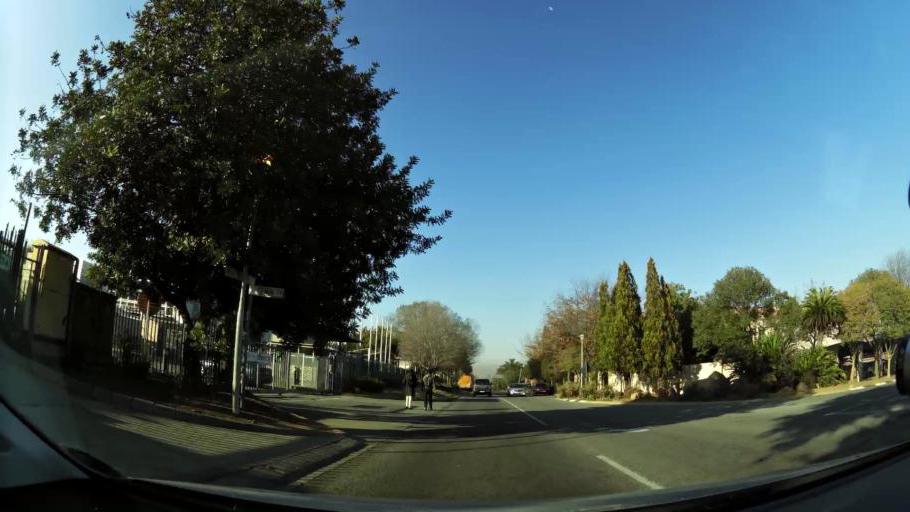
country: ZA
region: Gauteng
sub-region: City of Johannesburg Metropolitan Municipality
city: Modderfontein
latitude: -26.0695
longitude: 28.1161
